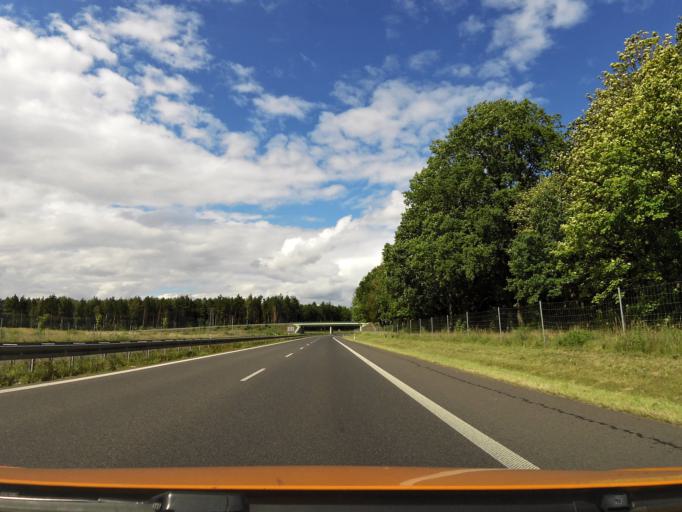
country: PL
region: West Pomeranian Voivodeship
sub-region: Powiat goleniowski
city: Nowogard
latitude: 53.6624
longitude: 15.0771
